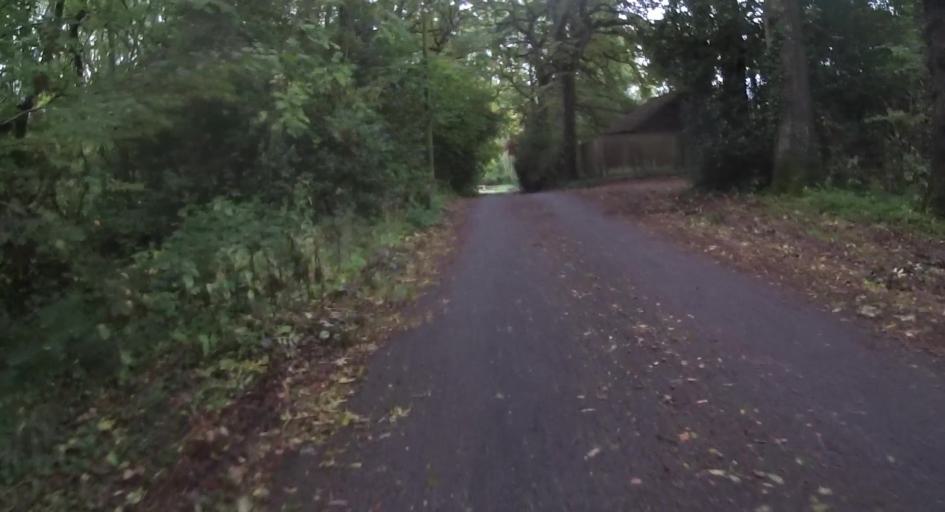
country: GB
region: England
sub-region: Hampshire
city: Tadley
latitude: 51.3543
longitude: -1.1777
